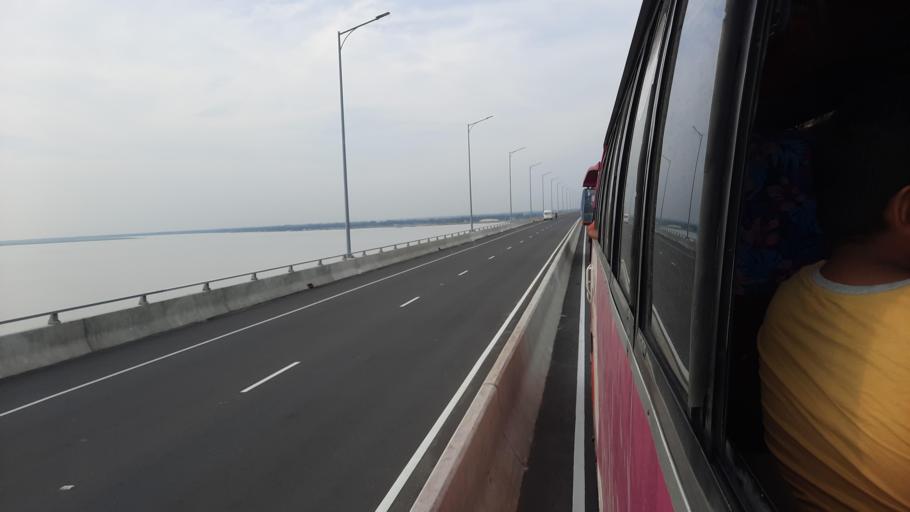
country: BD
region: Dhaka
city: Char Bhadrasan
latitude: 23.4502
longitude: 90.2616
